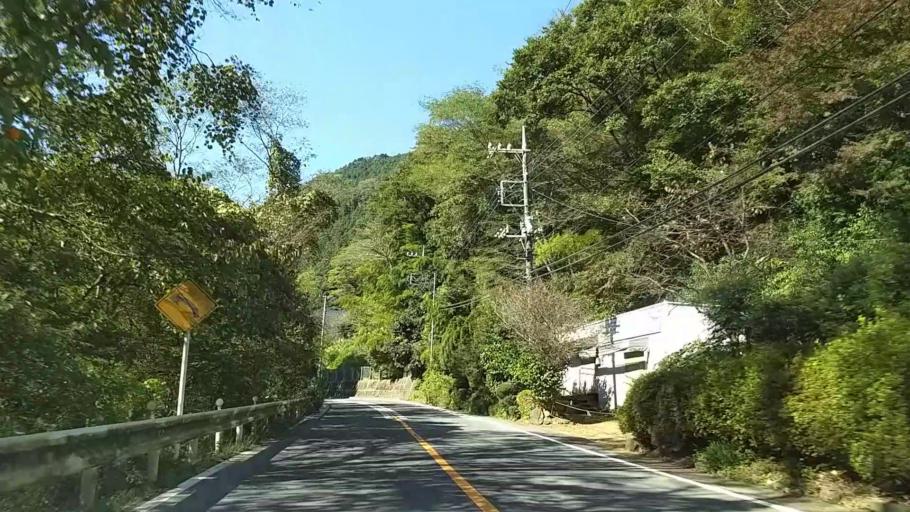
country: JP
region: Tokyo
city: Hachioji
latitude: 35.6192
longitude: 139.2564
